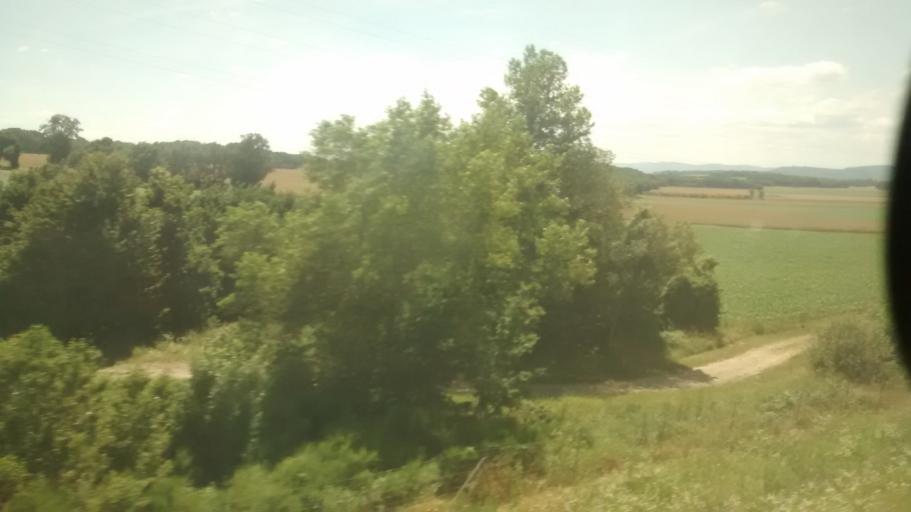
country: FR
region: Rhone-Alpes
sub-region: Departement de l'Ain
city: Saint-Maurice-de-Beynost
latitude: 45.8583
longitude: 4.9846
